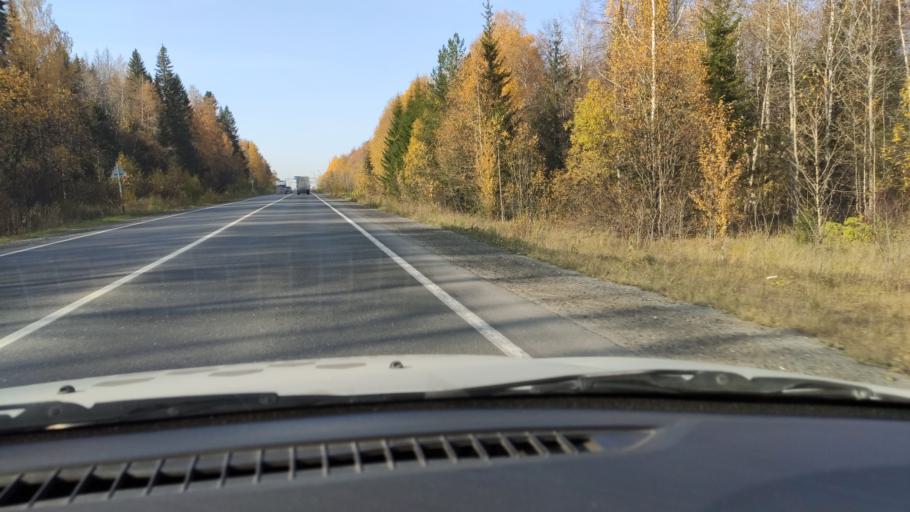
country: RU
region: Perm
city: Novyye Lyady
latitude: 58.0431
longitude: 56.4447
